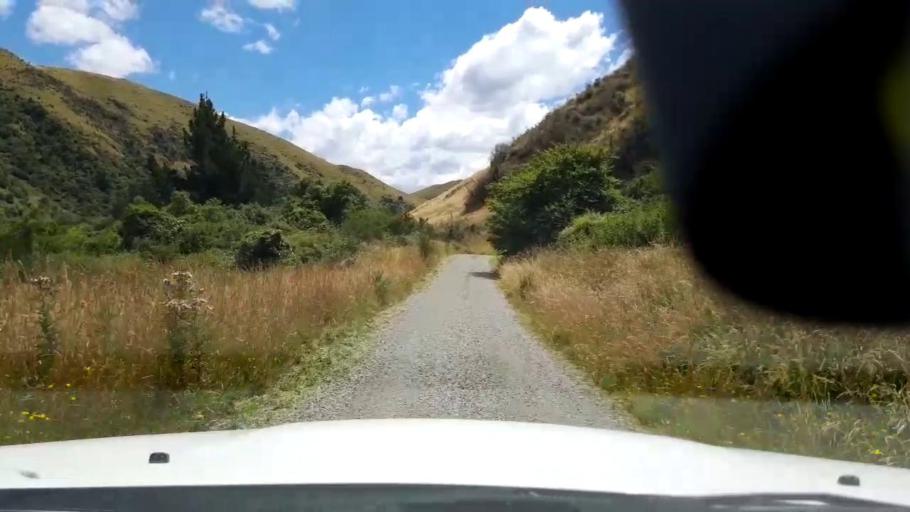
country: NZ
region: Canterbury
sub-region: Timaru District
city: Pleasant Point
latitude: -43.9337
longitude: 171.1978
